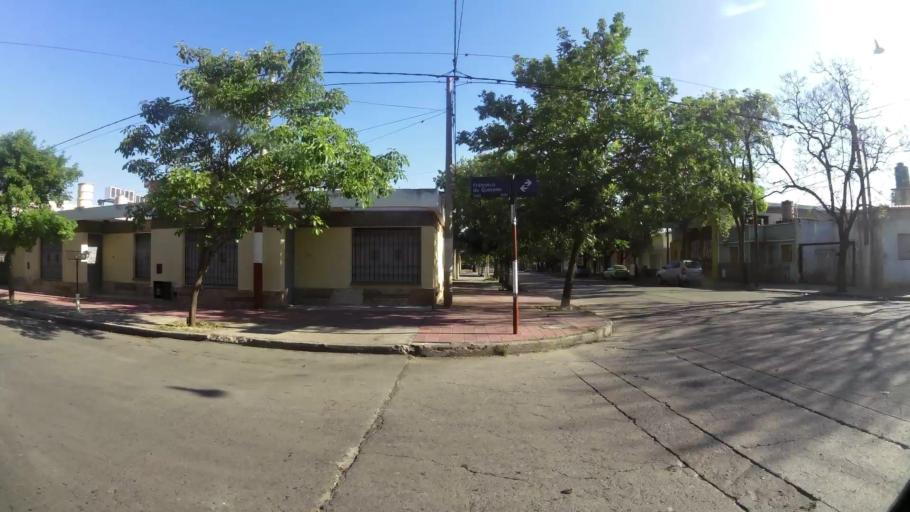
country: AR
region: Cordoba
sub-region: Departamento de Capital
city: Cordoba
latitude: -31.3841
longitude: -64.1771
